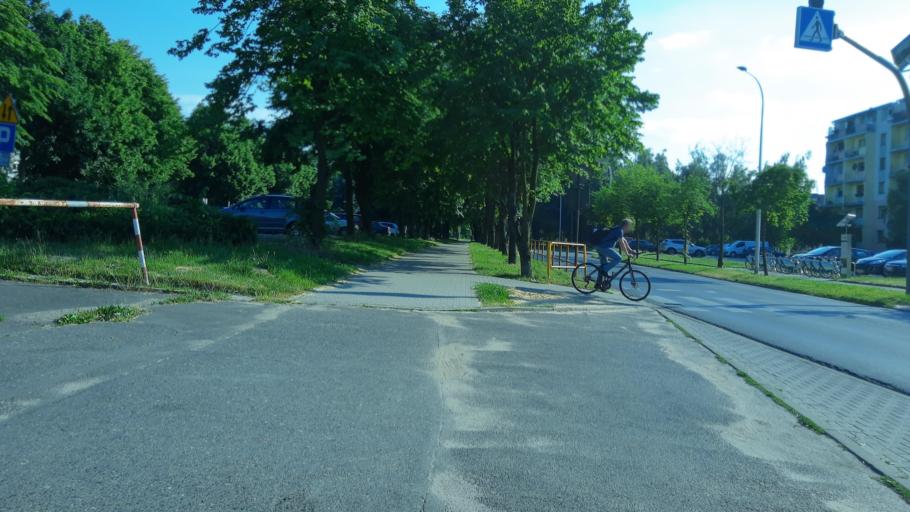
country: PL
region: Lodz Voivodeship
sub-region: Powiat sieradzki
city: Sieradz
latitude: 51.5832
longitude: 18.7099
